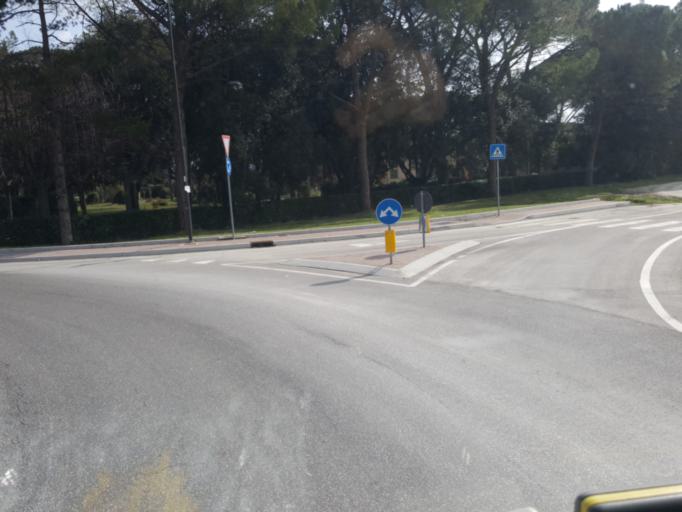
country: IT
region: The Marches
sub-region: Provincia di Macerata
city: Passo di Treia
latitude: 43.2878
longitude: 13.3337
